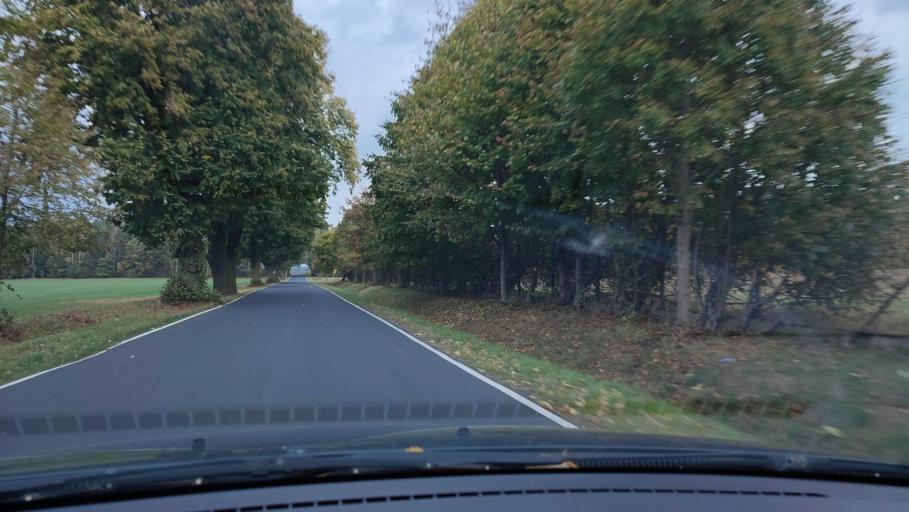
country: PL
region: Masovian Voivodeship
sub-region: Powiat mlawski
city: Wieczfnia Koscielna
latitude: 53.2159
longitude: 20.4049
